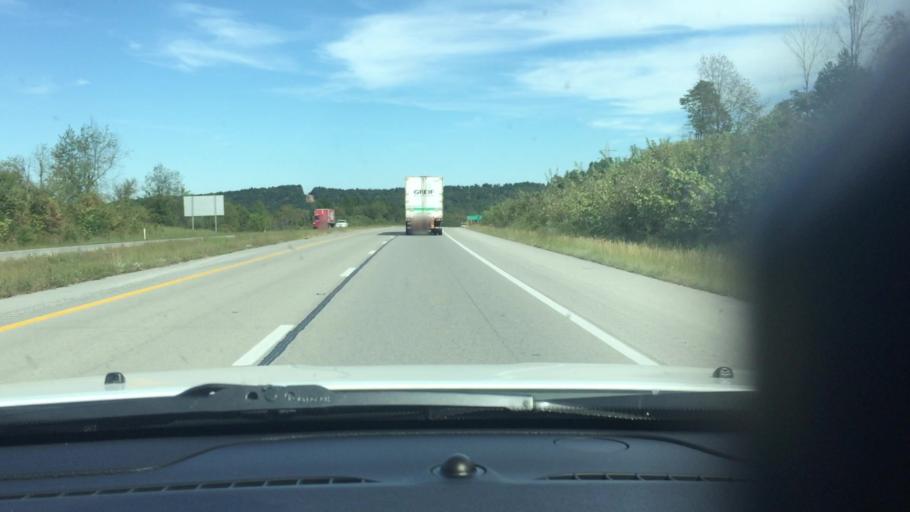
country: US
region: Kentucky
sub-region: Caldwell County
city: Princeton
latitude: 37.1380
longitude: -87.8554
